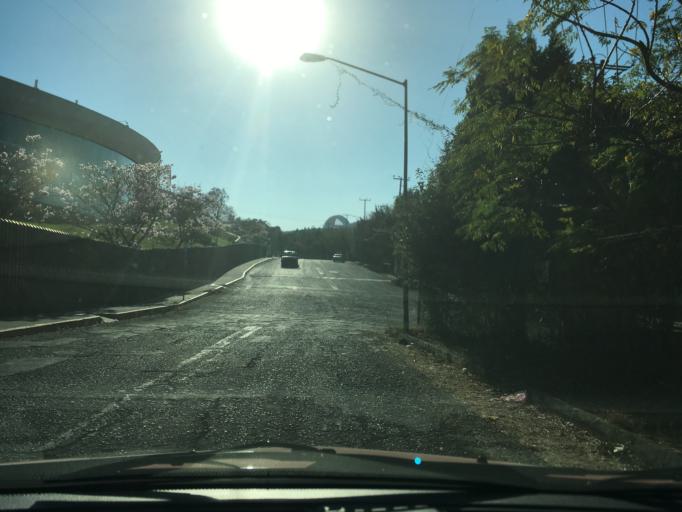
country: MX
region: Jalisco
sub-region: Tlajomulco de Zuniga
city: Altus Bosques
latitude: 20.6149
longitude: -103.3844
